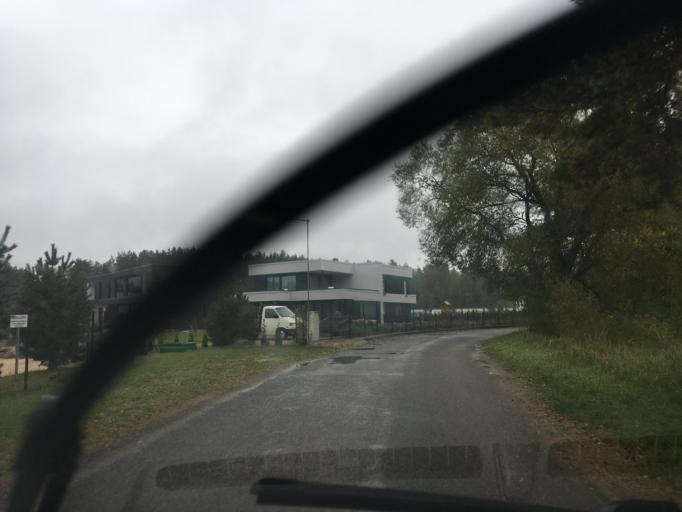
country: EE
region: Tartu
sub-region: UElenurme vald
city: Ulenurme
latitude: 58.3441
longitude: 26.7985
